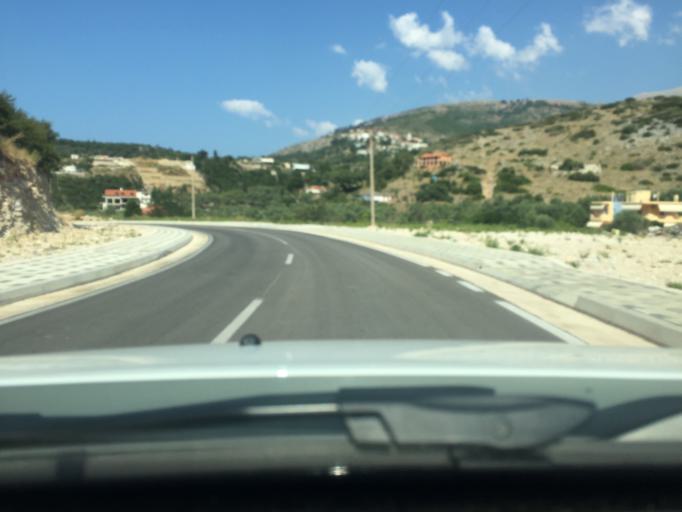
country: AL
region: Vlore
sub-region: Rrethi i Vlores
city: Himare
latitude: 40.1108
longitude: 19.7455
